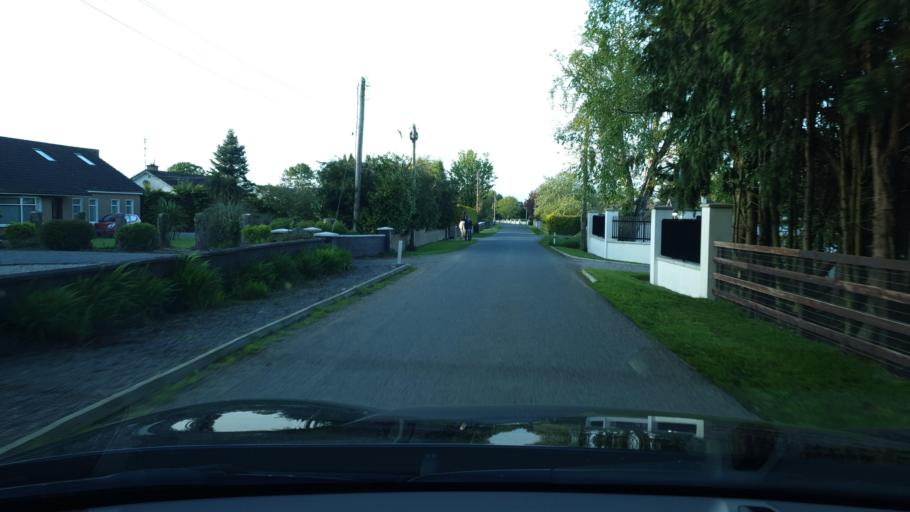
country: IE
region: Leinster
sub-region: An Mhi
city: Ashbourne
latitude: 53.4852
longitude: -6.4017
